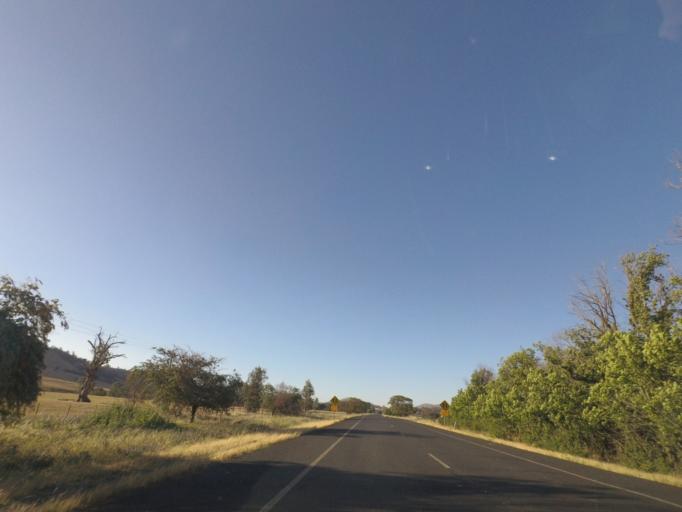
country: AU
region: New South Wales
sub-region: Gundagai
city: Gundagai
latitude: -34.9376
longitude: 148.1676
